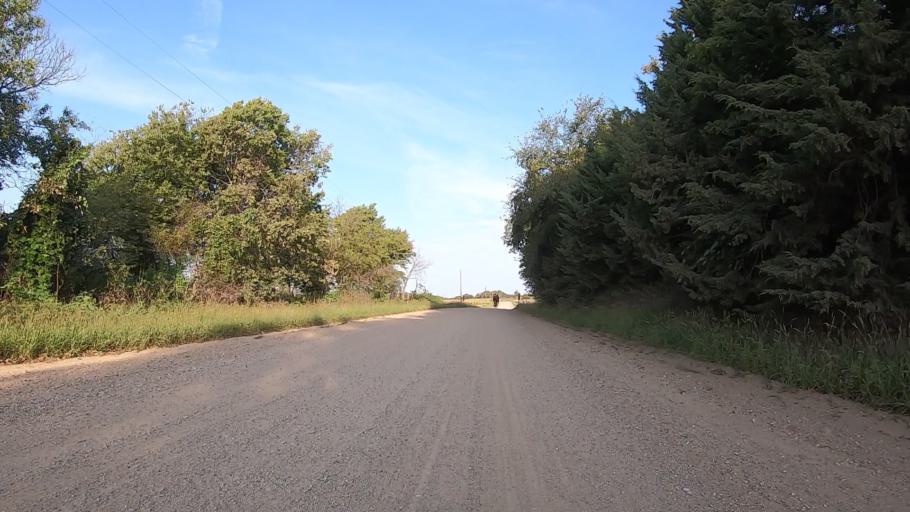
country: US
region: Kansas
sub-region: Marshall County
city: Blue Rapids
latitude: 39.7240
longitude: -96.7830
